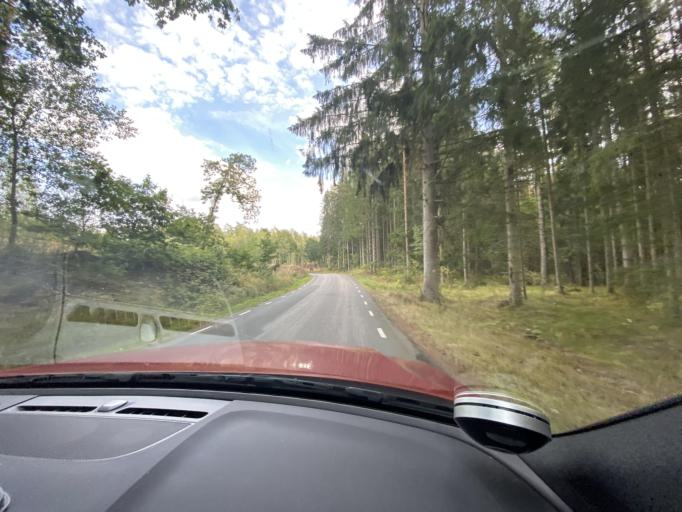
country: SE
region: Skane
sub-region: Hassleholms Kommun
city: Bjarnum
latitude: 56.3582
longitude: 13.8033
